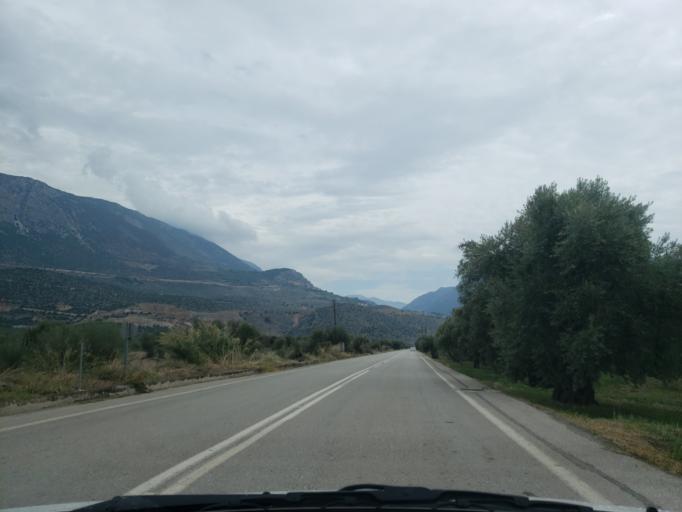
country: GR
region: Central Greece
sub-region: Nomos Fokidos
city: Kirra
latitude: 38.4807
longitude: 22.4357
